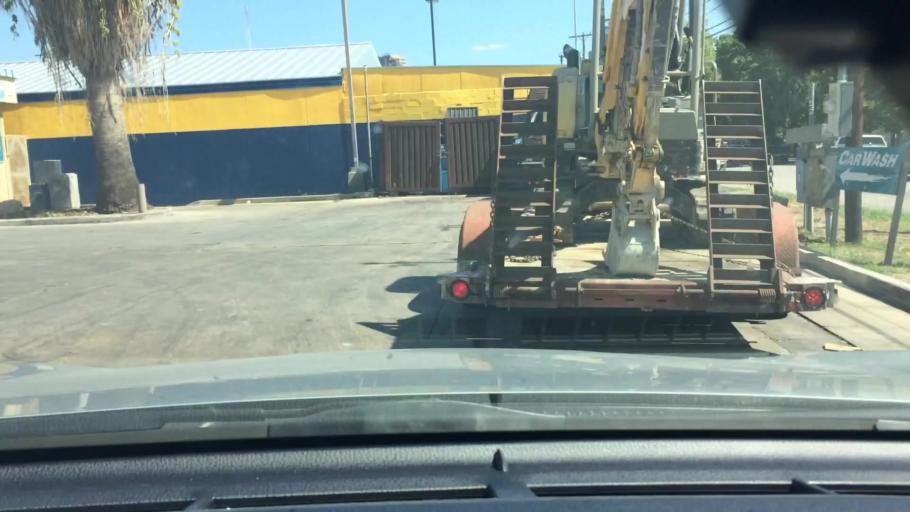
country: US
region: Texas
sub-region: Bexar County
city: San Antonio
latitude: 29.4363
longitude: -98.4970
